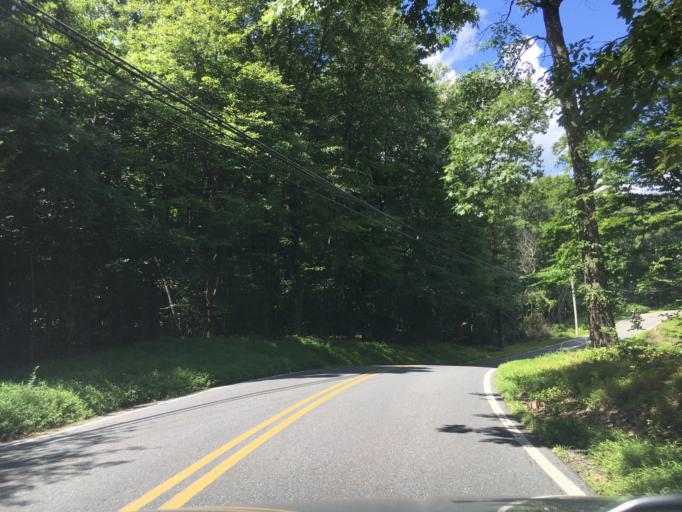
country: US
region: Pennsylvania
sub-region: Berks County
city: Fleetwood
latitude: 40.4441
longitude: -75.8007
